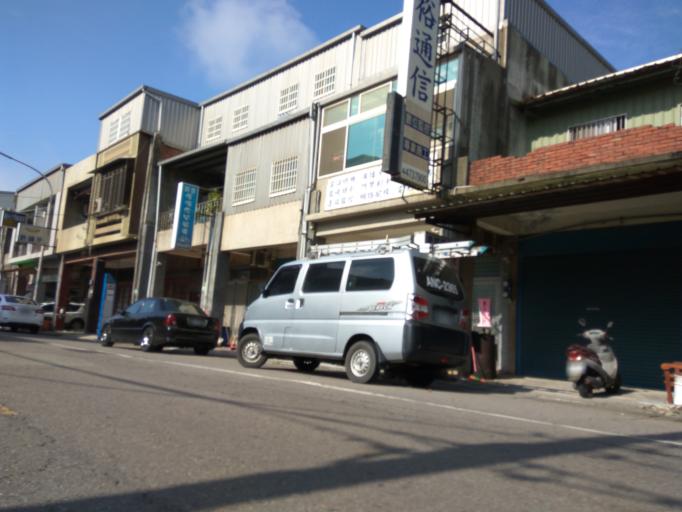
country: TW
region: Taiwan
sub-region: Hsinchu
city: Zhubei
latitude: 25.0356
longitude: 121.0839
